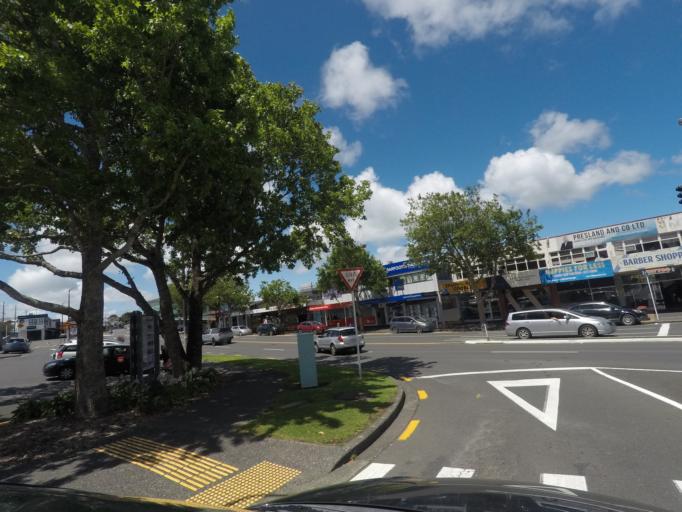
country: NZ
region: Auckland
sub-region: Auckland
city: Waitakere
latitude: -36.9102
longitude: 174.6523
